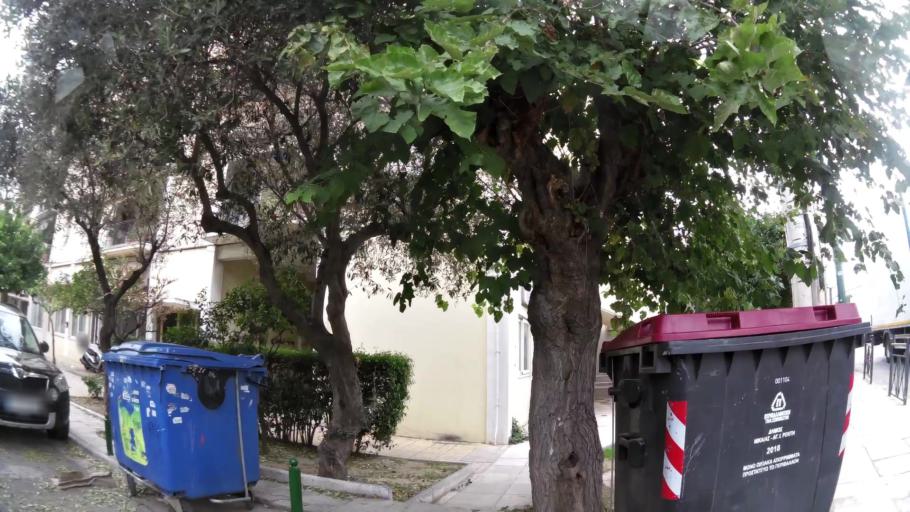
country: GR
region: Attica
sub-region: Nomarchia Athinas
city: Tavros
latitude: 37.9758
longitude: 23.6848
